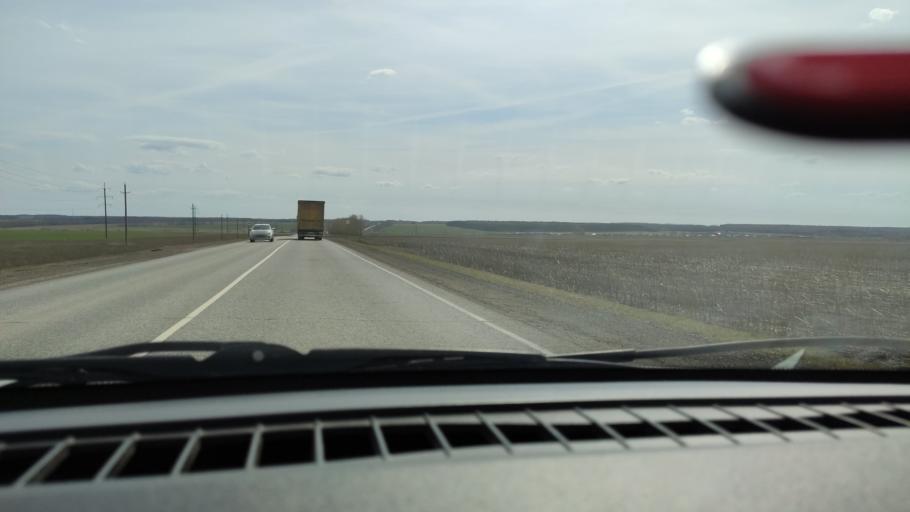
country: RU
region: Bashkortostan
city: Dyurtyuli
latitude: 55.3071
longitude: 55.0030
